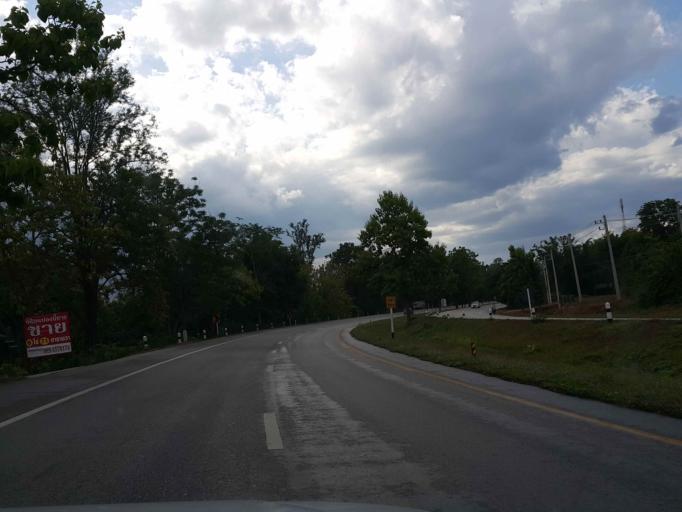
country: TH
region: Lampang
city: Thoen
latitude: 17.6622
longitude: 99.2453
